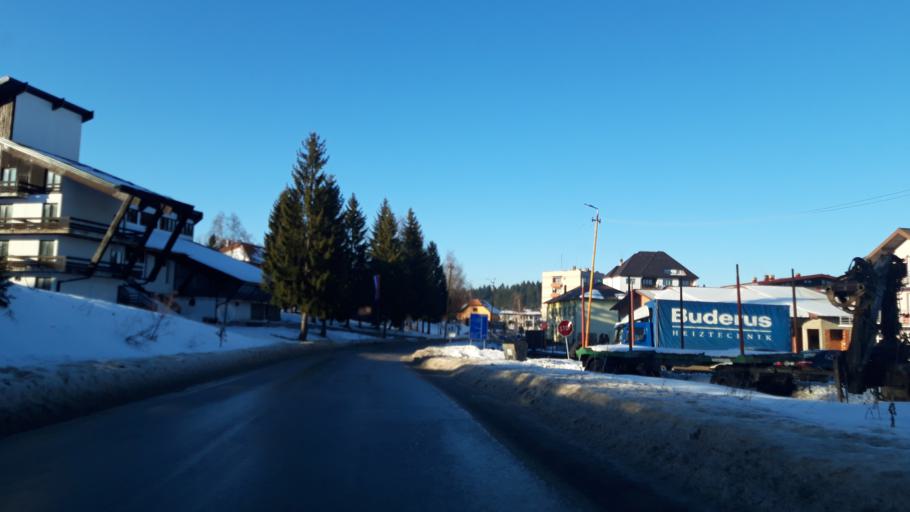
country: BA
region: Republika Srpska
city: Han Pijesak
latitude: 44.0793
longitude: 18.9527
